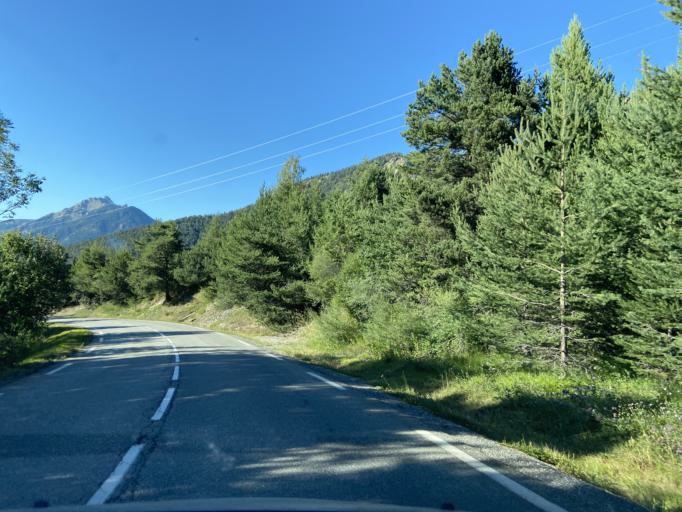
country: FR
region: Provence-Alpes-Cote d'Azur
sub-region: Departement des Hautes-Alpes
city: Guillestre
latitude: 44.6327
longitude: 6.6768
